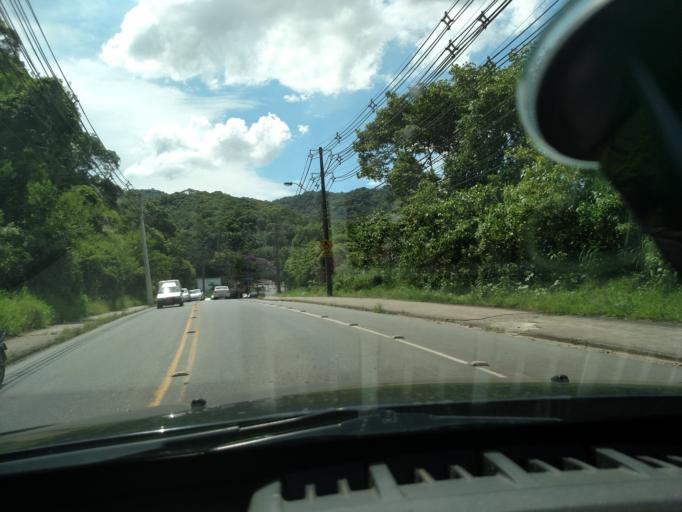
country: BR
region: Santa Catarina
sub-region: Blumenau
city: Blumenau
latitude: -26.9477
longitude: -49.0766
